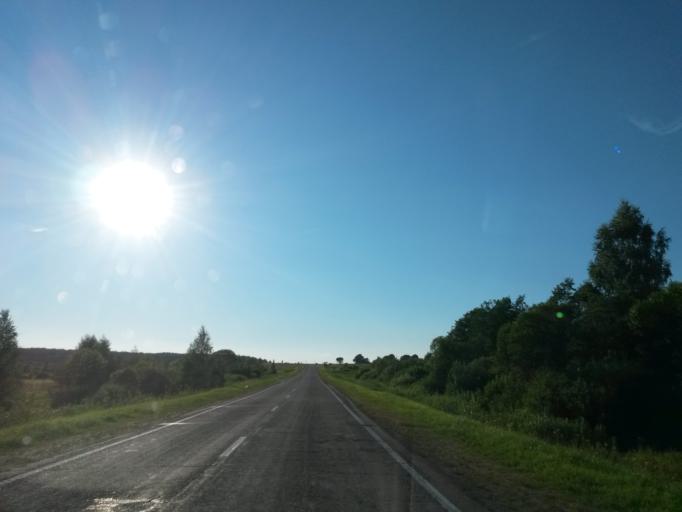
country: RU
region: Jaroslavl
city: Gavrilov-Yam
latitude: 57.2808
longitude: 39.9103
